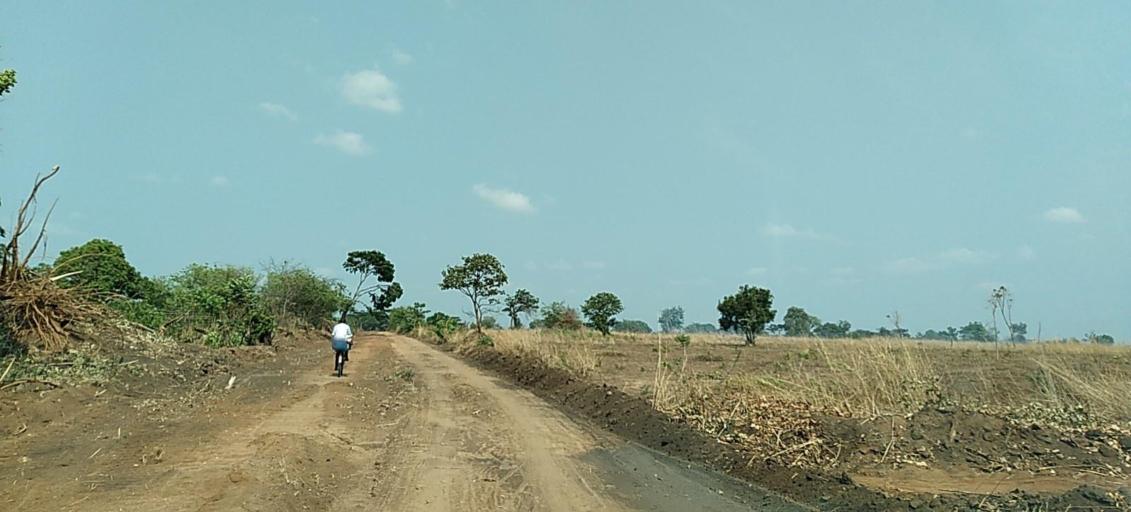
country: ZM
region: Copperbelt
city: Luanshya
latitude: -13.0895
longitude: 28.2656
